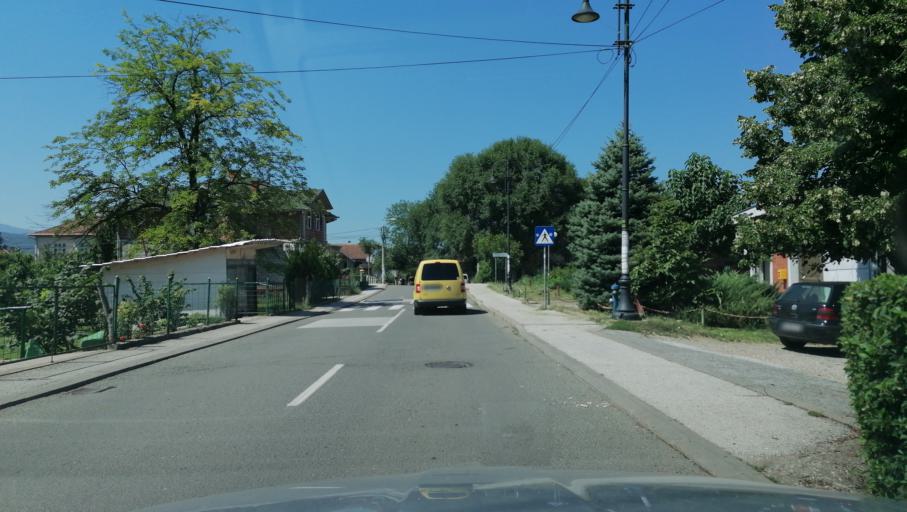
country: RS
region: Central Serbia
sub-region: Raski Okrug
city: Kraljevo
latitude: 43.6895
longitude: 20.6100
